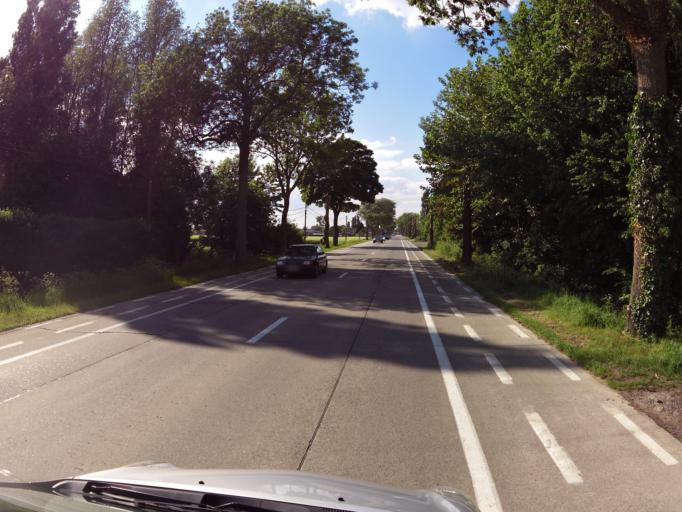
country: BE
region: Flanders
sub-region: Provincie West-Vlaanderen
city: Poperinge
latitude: 50.9262
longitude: 2.7462
